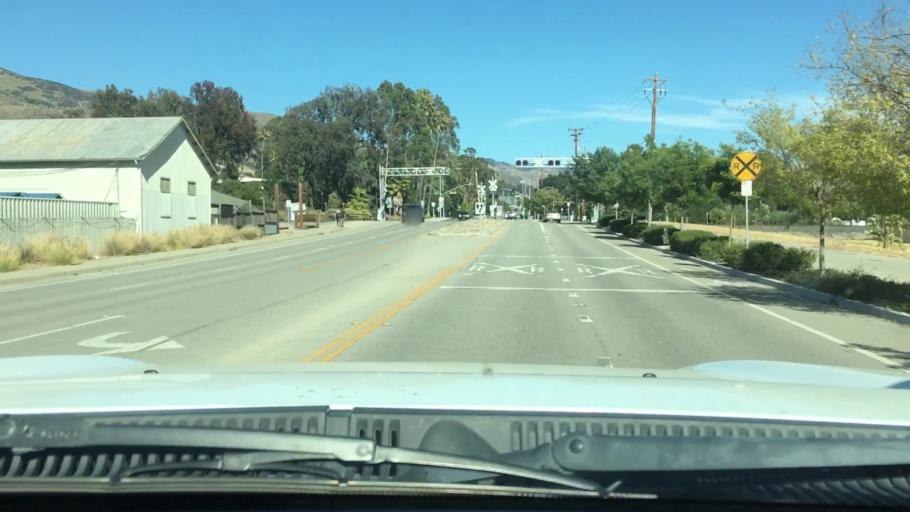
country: US
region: California
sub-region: San Luis Obispo County
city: San Luis Obispo
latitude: 35.2613
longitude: -120.6458
